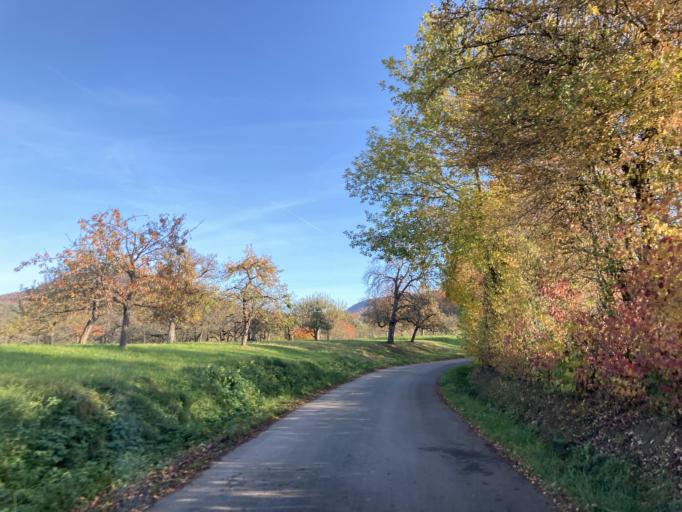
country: DE
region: Baden-Wuerttemberg
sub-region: Tuebingen Region
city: Mossingen
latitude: 48.3917
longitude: 9.0406
